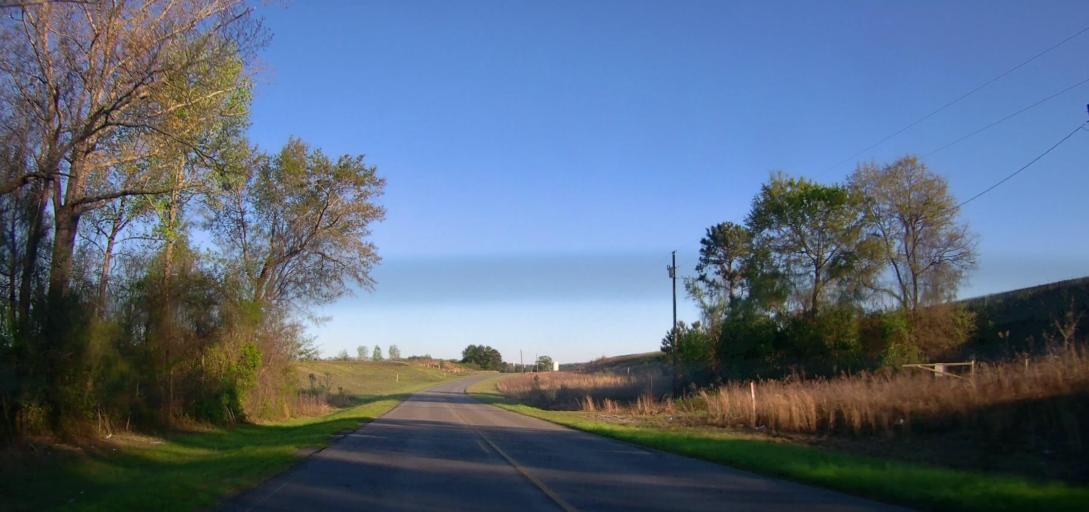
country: US
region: Georgia
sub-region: Wilkinson County
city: Irwinton
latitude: 32.8681
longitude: -83.2358
